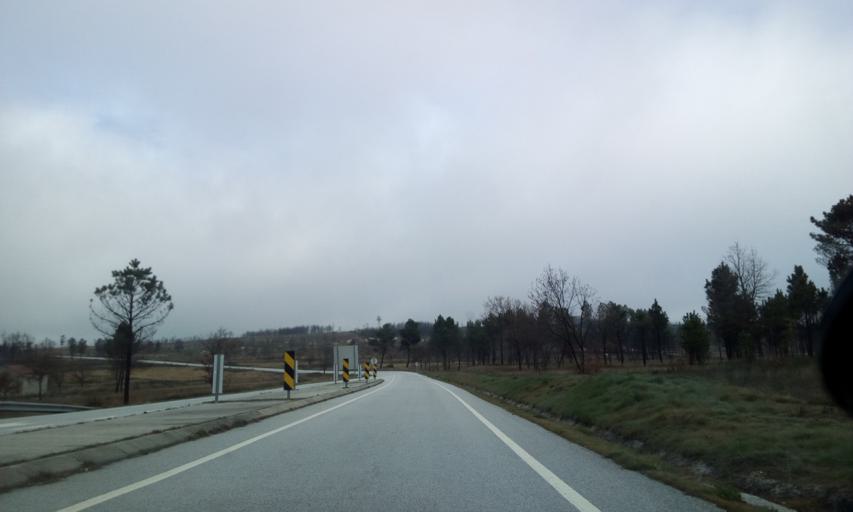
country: PT
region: Guarda
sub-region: Fornos de Algodres
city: Fornos de Algodres
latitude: 40.6960
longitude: -7.4736
